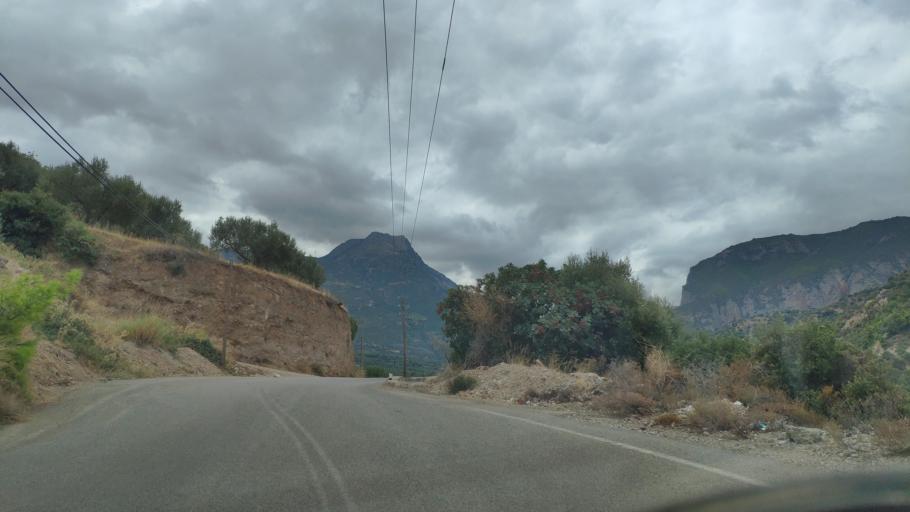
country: GR
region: West Greece
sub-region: Nomos Achaias
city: Temeni
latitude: 38.1867
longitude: 22.1489
